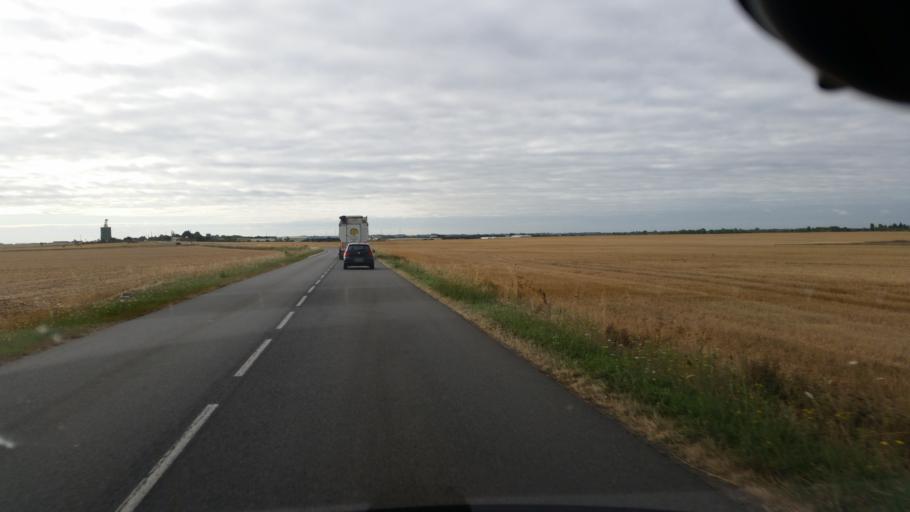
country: FR
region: Poitou-Charentes
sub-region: Departement de la Charente-Maritime
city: Marans
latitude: 46.2944
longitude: -0.9676
